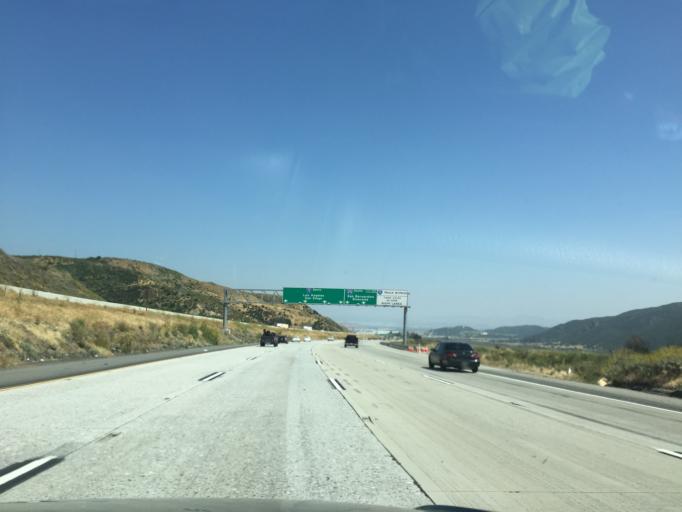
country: US
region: California
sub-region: San Bernardino County
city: Muscoy
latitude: 34.2477
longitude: -117.4391
